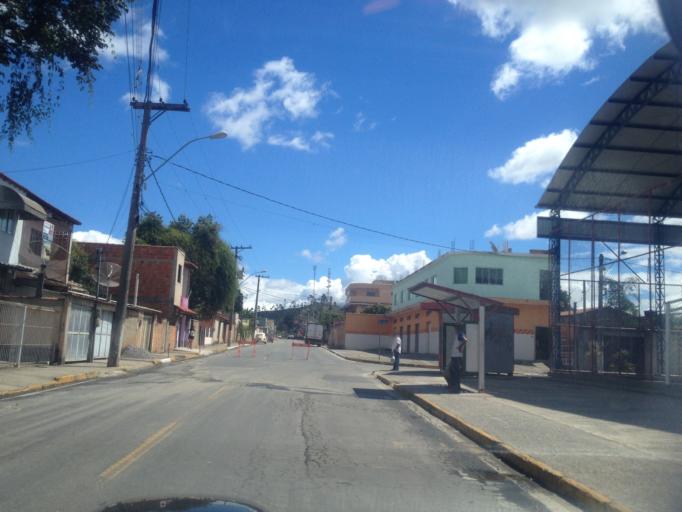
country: BR
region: Rio de Janeiro
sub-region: Porto Real
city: Porto Real
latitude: -22.4444
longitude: -44.3125
